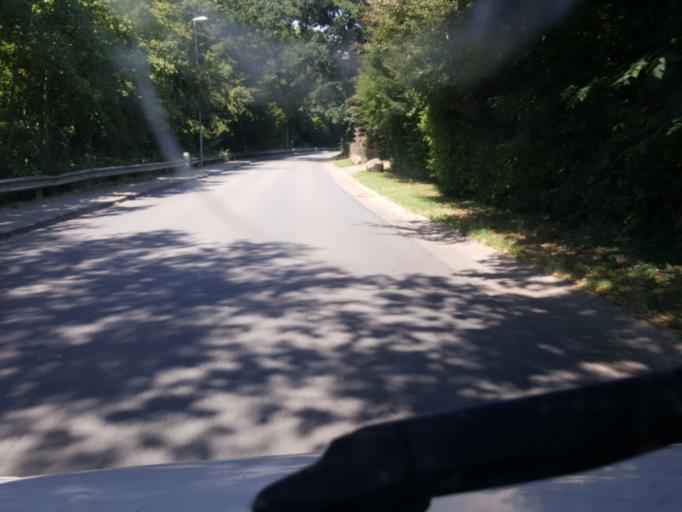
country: DE
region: North Rhine-Westphalia
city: Bad Oeynhausen
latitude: 52.2480
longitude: 8.7427
